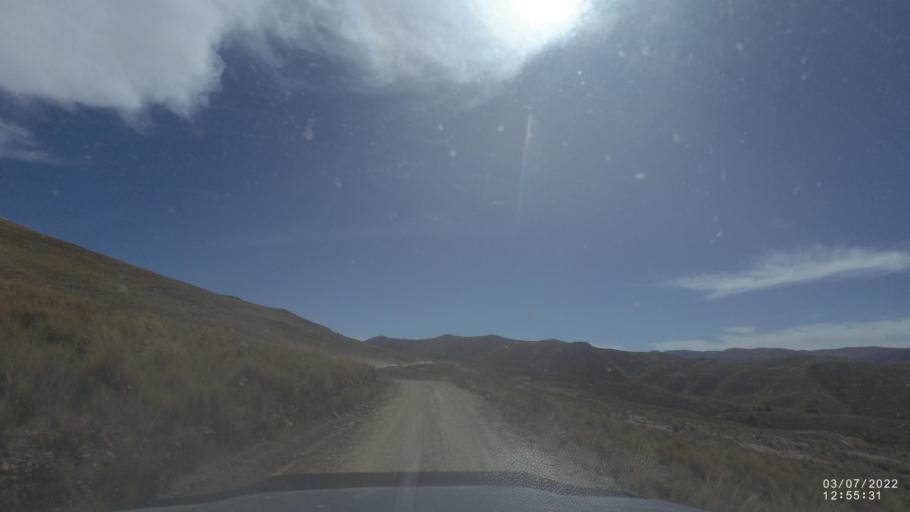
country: BO
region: Cochabamba
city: Sipe Sipe
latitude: -17.7331
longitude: -66.6702
